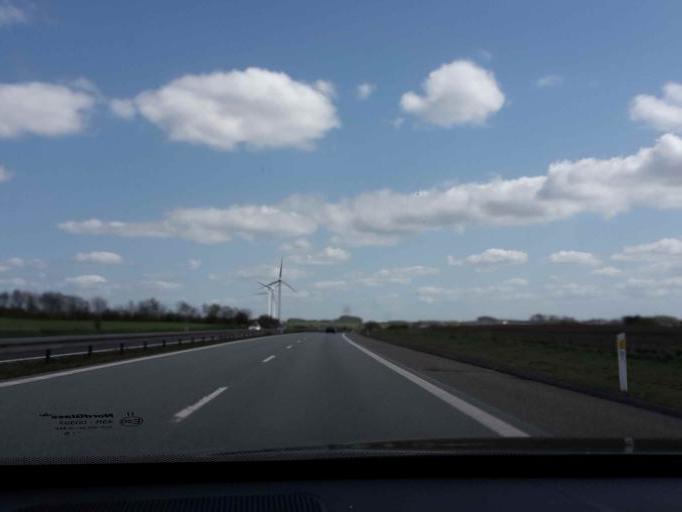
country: DK
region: South Denmark
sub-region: Vejen Kommune
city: Brorup
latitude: 55.5097
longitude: 8.9860
